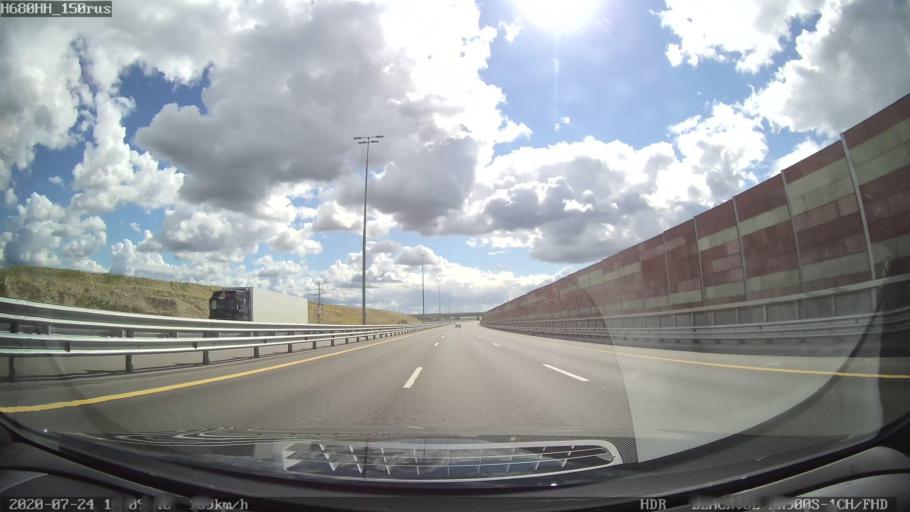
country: RU
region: St.-Petersburg
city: Tyarlevo
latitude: 59.7475
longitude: 30.4815
